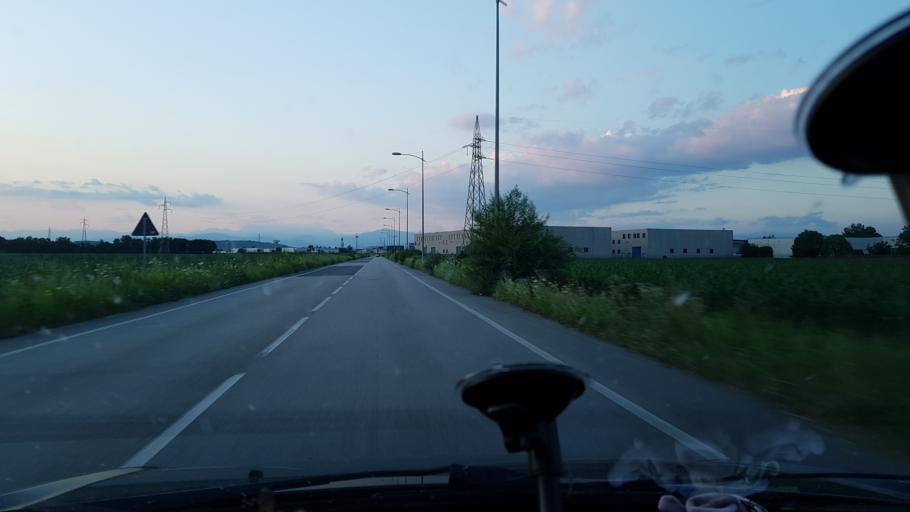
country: IT
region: Friuli Venezia Giulia
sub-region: Provincia di Gorizia
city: Villesse
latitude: 45.8725
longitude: 13.4350
